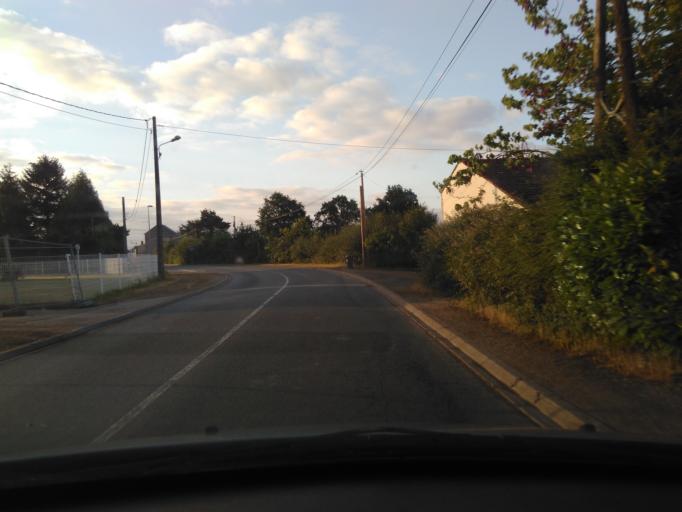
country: FR
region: Pays de la Loire
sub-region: Departement de la Vendee
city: Mouilleron-le-Captif
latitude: 46.7320
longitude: -1.4400
